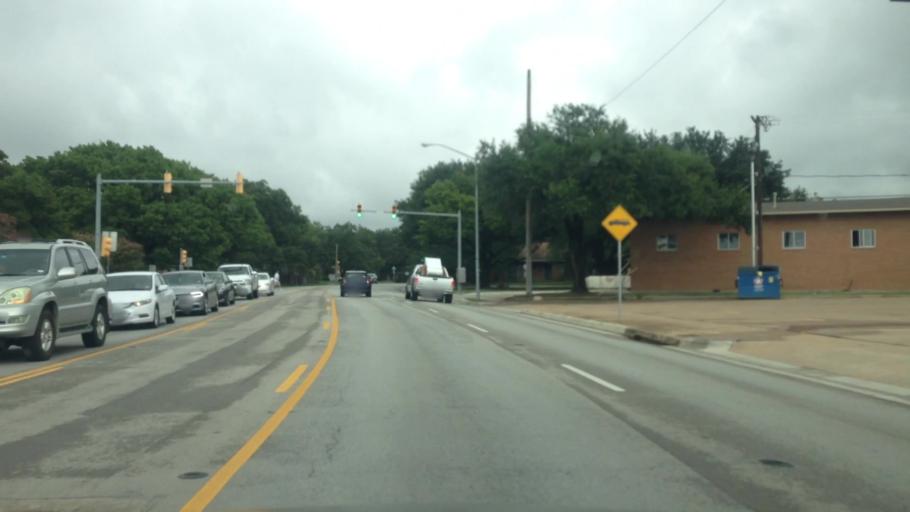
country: US
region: Texas
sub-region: Tarrant County
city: Edgecliff Village
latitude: 32.6588
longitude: -97.3988
